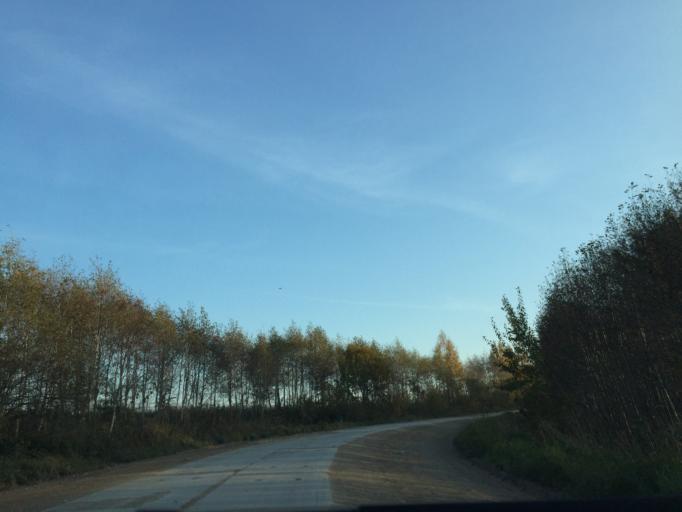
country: LV
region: Vainode
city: Vainode
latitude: 56.5532
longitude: 21.8425
